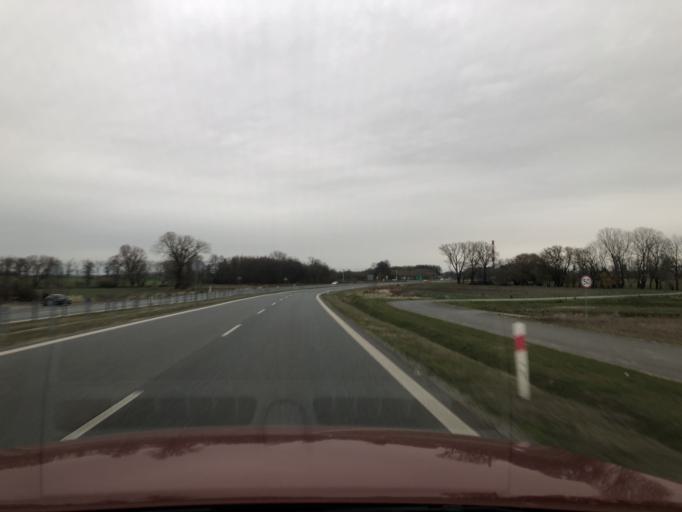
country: PL
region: Lower Silesian Voivodeship
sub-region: Powiat swidnicki
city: Swidnica
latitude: 50.8587
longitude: 16.4513
